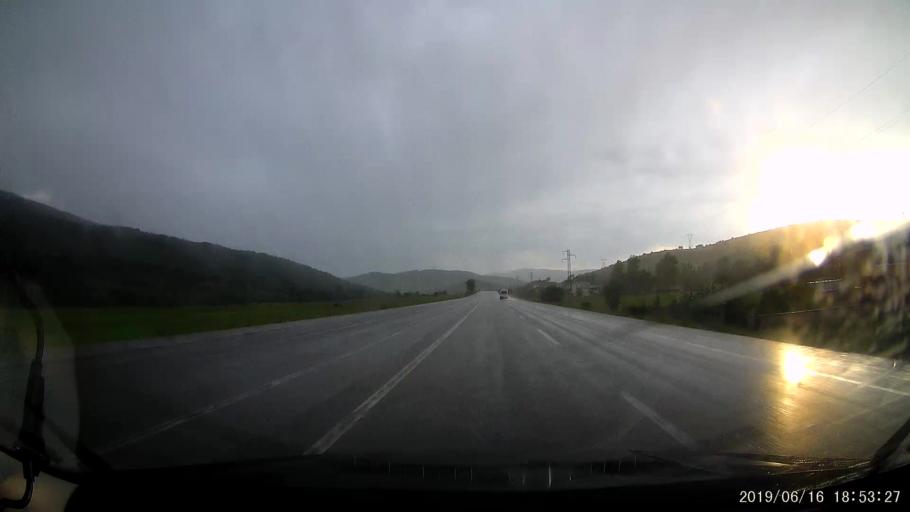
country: TR
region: Erzincan
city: Catalcam
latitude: 39.8985
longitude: 38.8775
